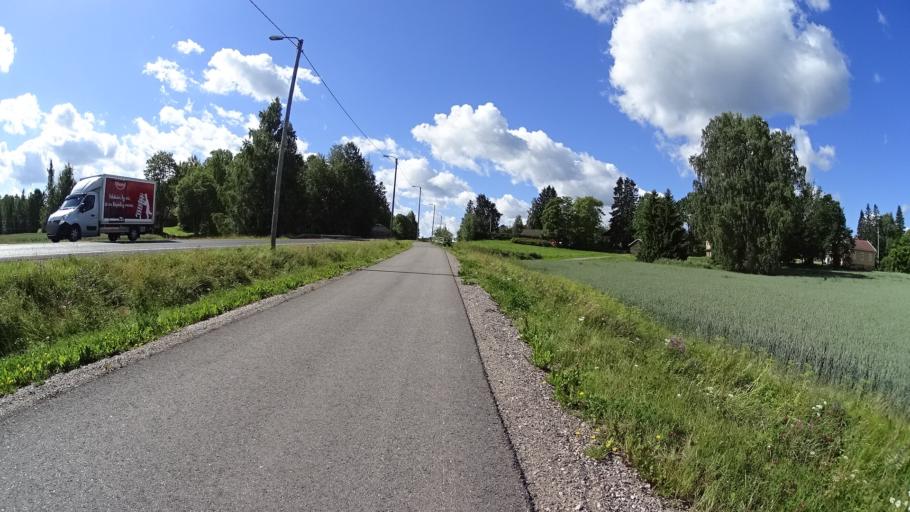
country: FI
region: Uusimaa
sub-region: Helsinki
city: Jaervenpaeae
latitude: 60.4401
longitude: 25.0716
